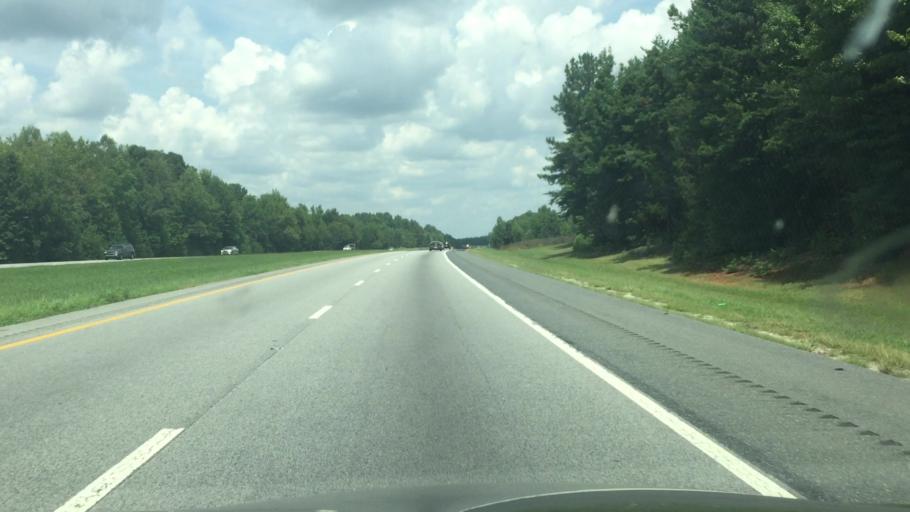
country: US
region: North Carolina
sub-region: Guilford County
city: Pleasant Garden
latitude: 35.9396
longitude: -79.8262
